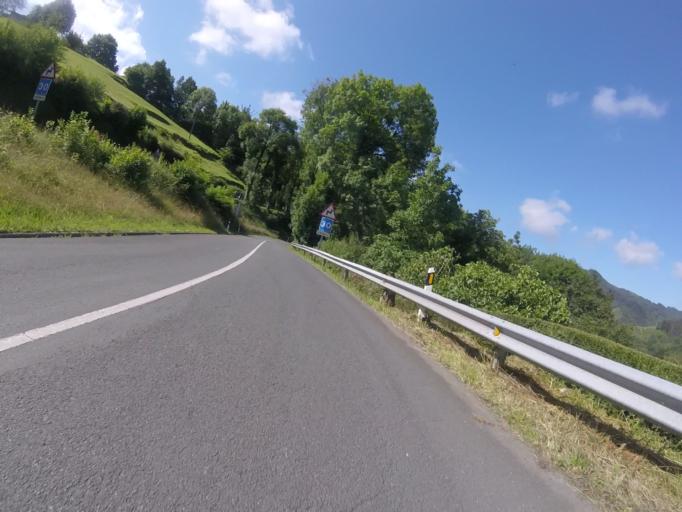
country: ES
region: Basque Country
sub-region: Provincia de Guipuzcoa
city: Beizama
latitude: 43.1000
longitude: -2.2402
